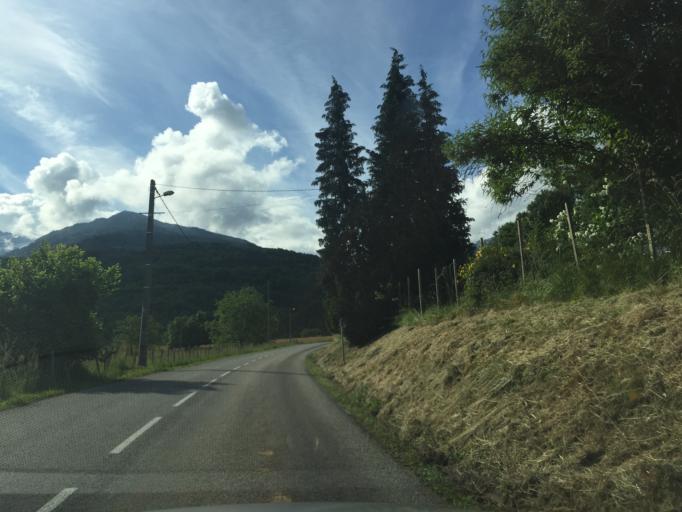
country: FR
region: Rhone-Alpes
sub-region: Departement de la Savoie
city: La Rochette
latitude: 45.4479
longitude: 6.1207
